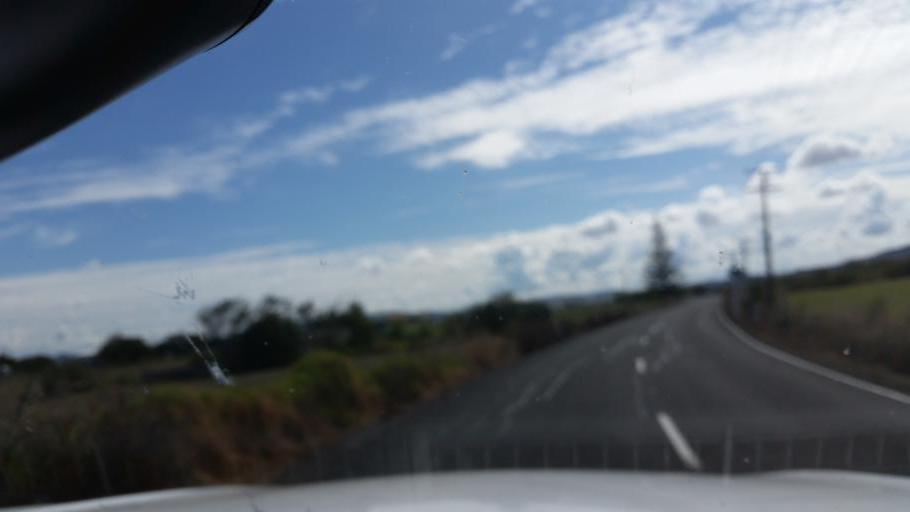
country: NZ
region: Northland
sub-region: Kaipara District
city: Dargaville
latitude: -36.1490
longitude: 174.0663
